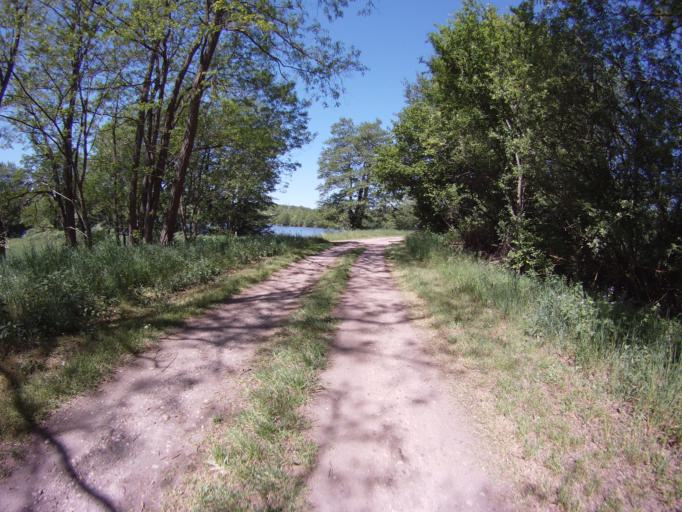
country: FR
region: Lorraine
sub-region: Departement de Meurthe-et-Moselle
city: Dommartin-les-Toul
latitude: 48.6549
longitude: 5.9003
